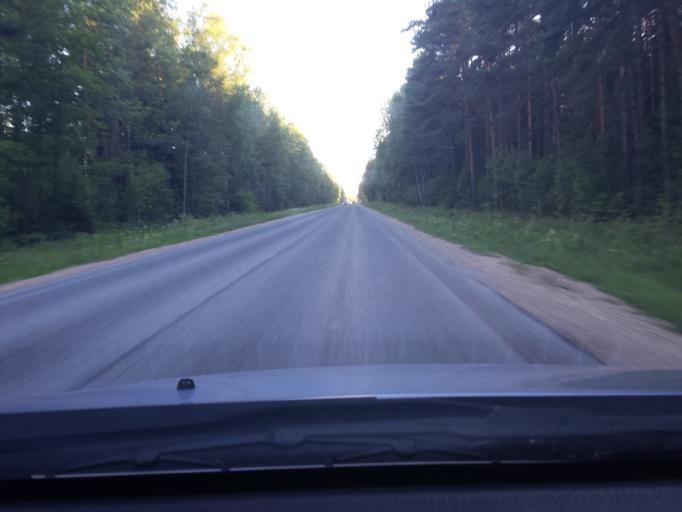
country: LV
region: Carnikava
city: Carnikava
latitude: 57.1070
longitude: 24.2202
